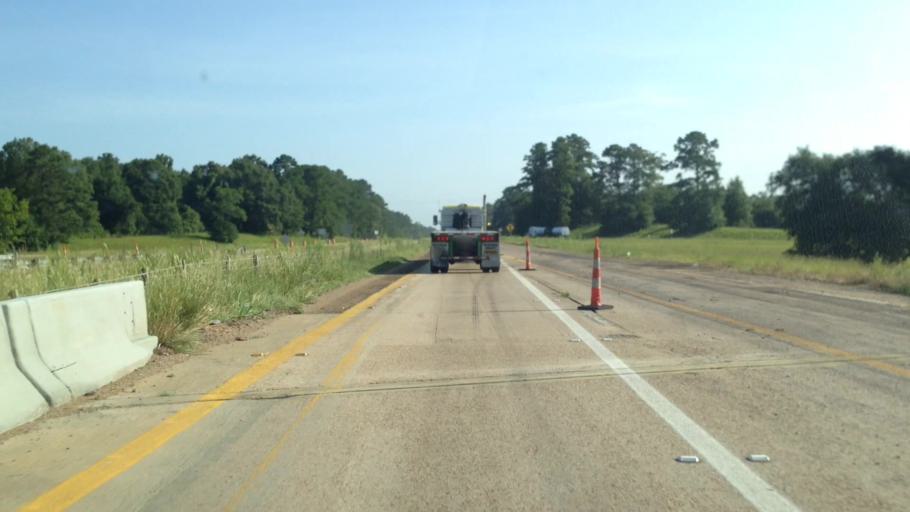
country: US
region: Mississippi
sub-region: Pike County
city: McComb
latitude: 31.2214
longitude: -90.4828
